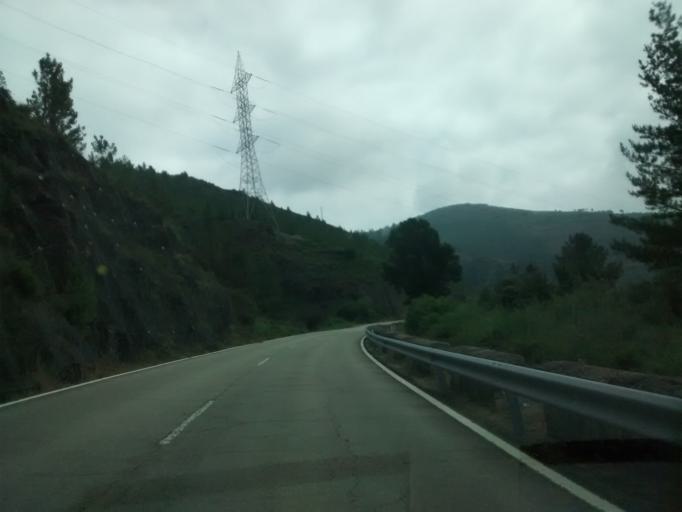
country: ES
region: Galicia
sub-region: Provincia de Ourense
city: Manzaneda
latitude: 42.3300
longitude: -7.2043
